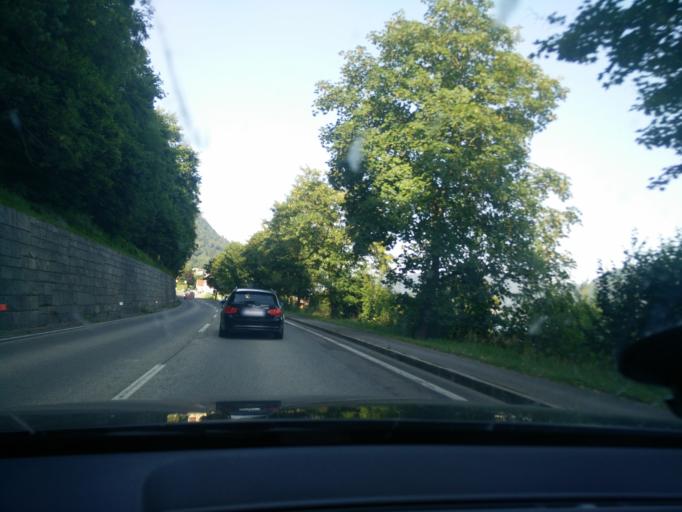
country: AT
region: Carinthia
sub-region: Politischer Bezirk Villach Land
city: Wernberg
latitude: 46.6612
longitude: 13.9101
